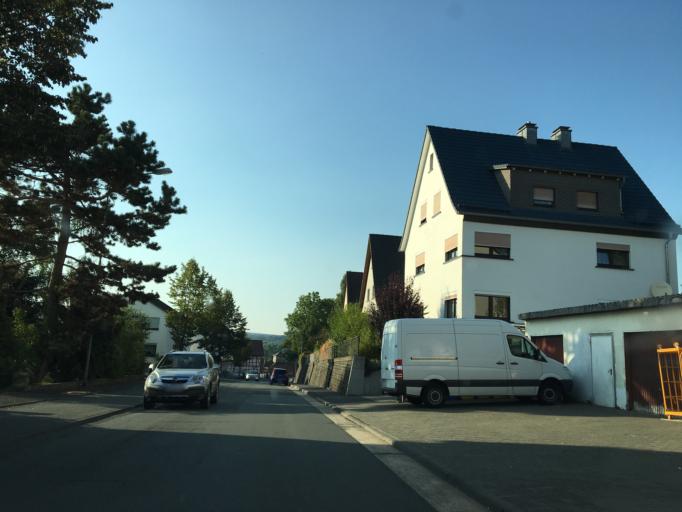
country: DE
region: Hesse
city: Frankenberg
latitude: 51.0527
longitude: 8.7917
